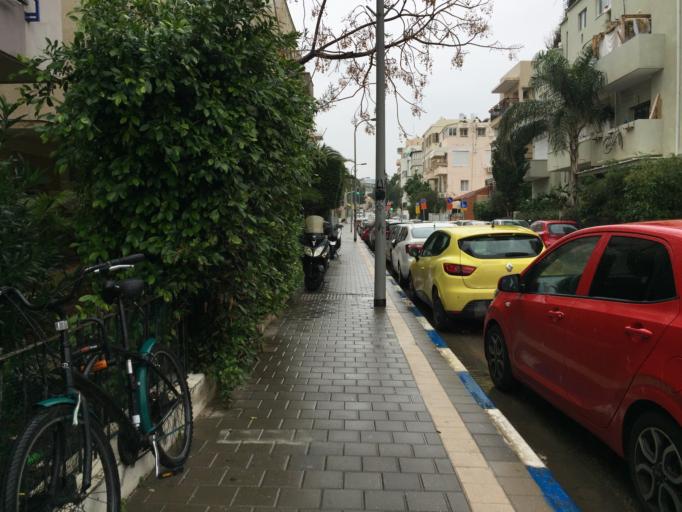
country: IL
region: Tel Aviv
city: Tel Aviv
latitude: 32.0715
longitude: 34.7659
